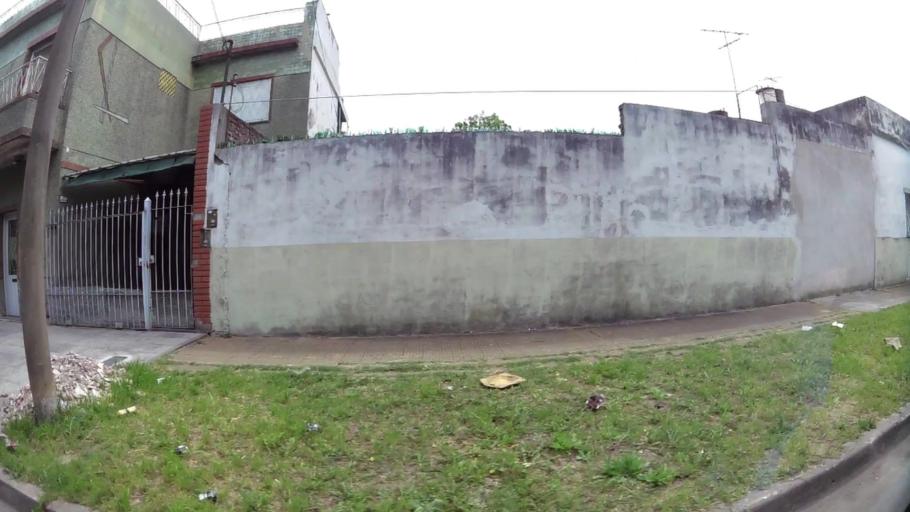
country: AR
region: Buenos Aires
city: San Justo
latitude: -34.6701
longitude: -58.5453
